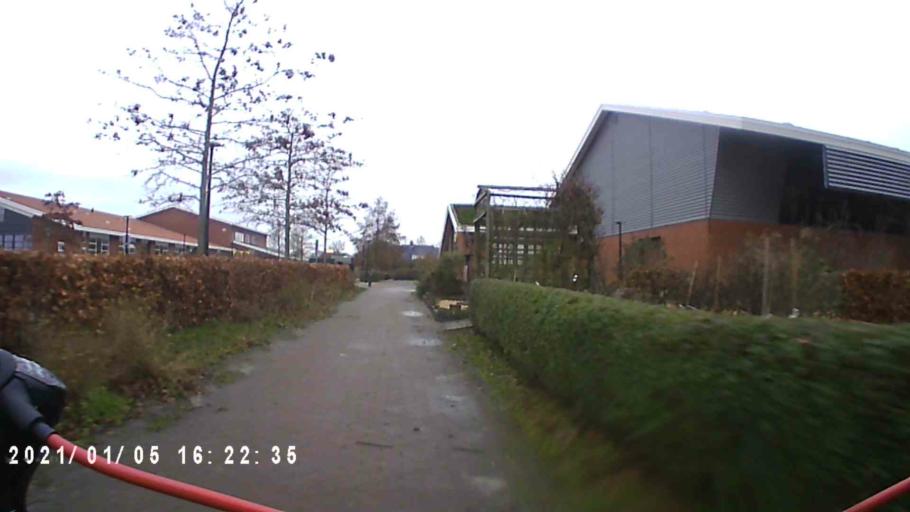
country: NL
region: Groningen
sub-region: Gemeente  Oldambt
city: Winschoten
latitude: 53.1990
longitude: 7.0388
